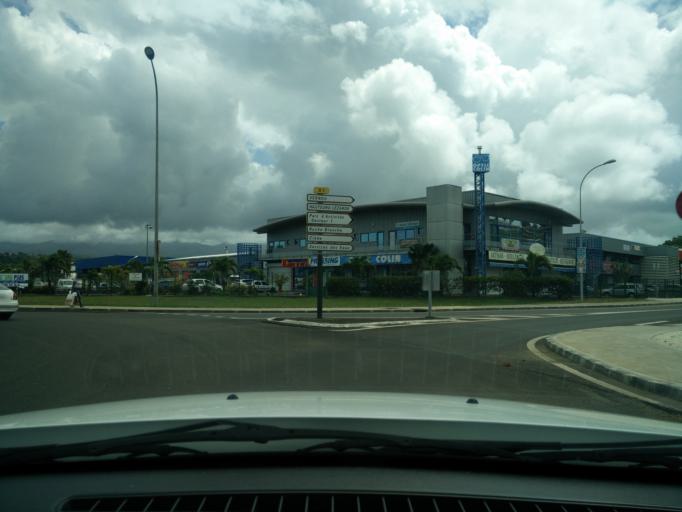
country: GP
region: Guadeloupe
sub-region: Guadeloupe
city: Petit-Bourg
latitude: 16.2029
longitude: -61.6070
